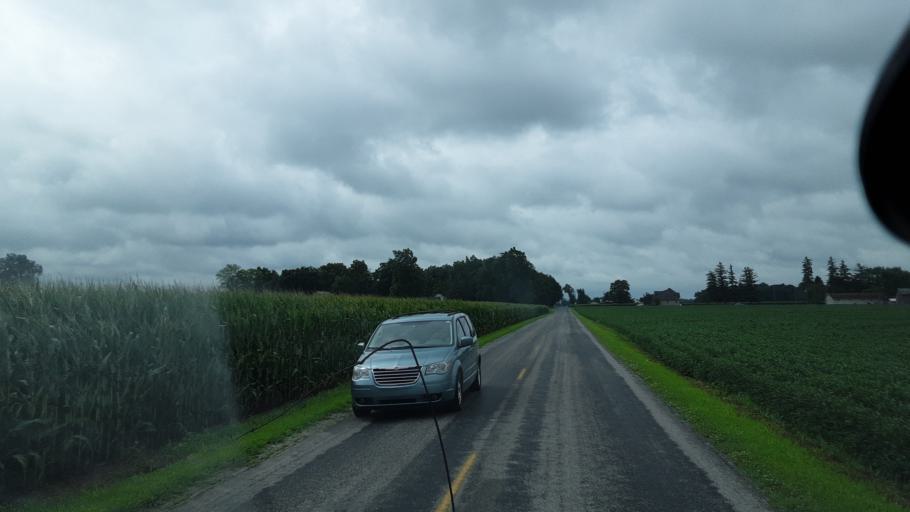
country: US
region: Indiana
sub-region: Wells County
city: Ossian
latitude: 40.8627
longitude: -85.1093
